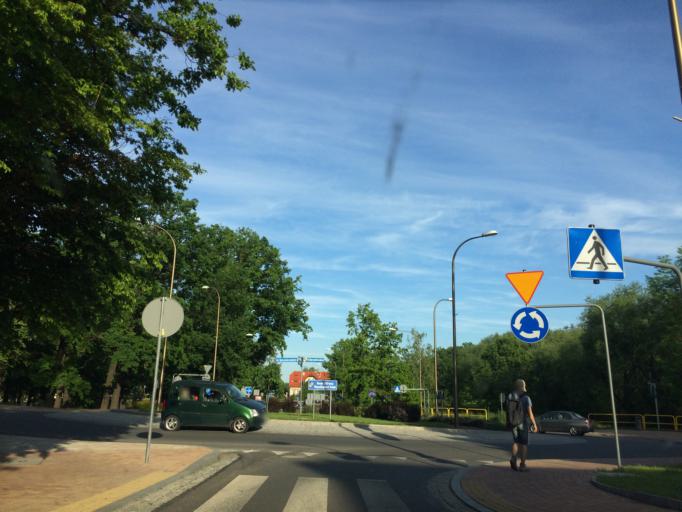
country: PL
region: Lower Silesian Voivodeship
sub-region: Powiat swidnicki
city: Swidnica
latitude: 50.8358
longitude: 16.4849
